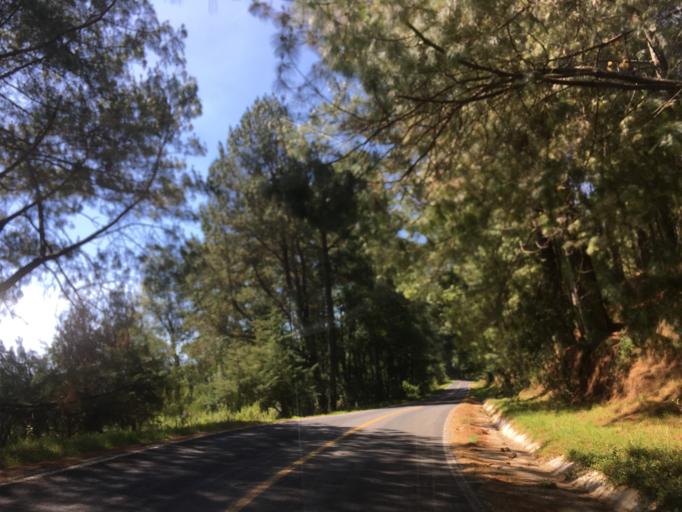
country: MX
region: Michoacan
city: Tzitzio
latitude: 19.6616
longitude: -100.8038
